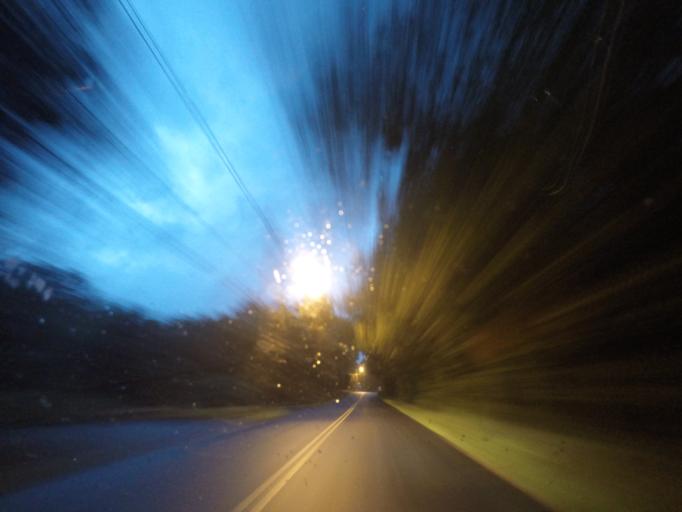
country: US
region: Massachusetts
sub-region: Worcester County
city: Sturbridge
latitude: 42.0698
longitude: -72.0961
